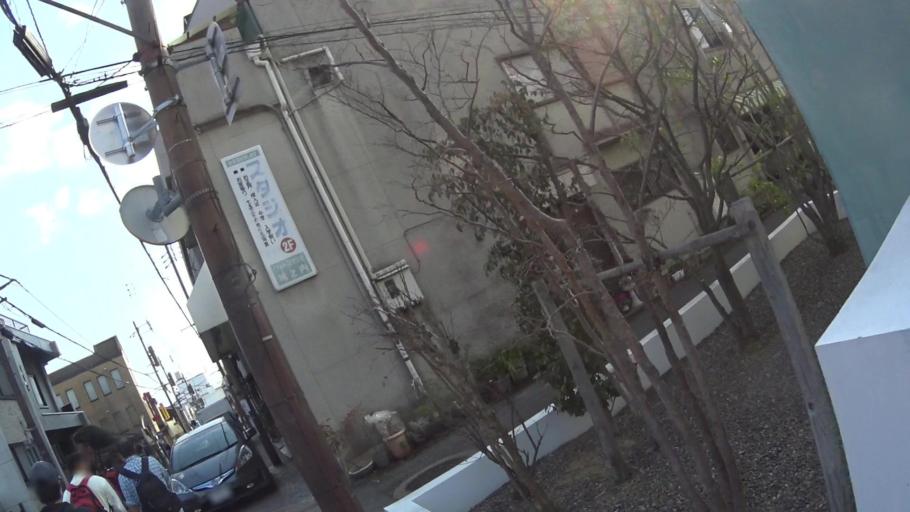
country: JP
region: Nara
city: Nara-shi
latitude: 34.6858
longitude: 135.8214
